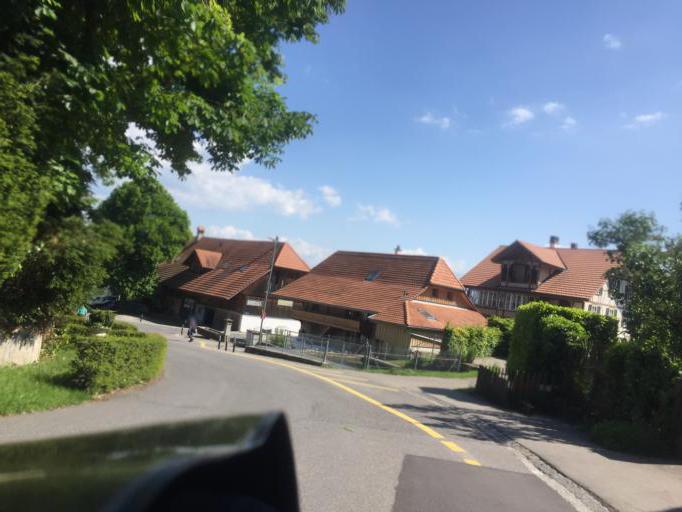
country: CH
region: Bern
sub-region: Bern-Mittelland District
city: Niederwichtrach
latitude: 46.8408
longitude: 7.5438
